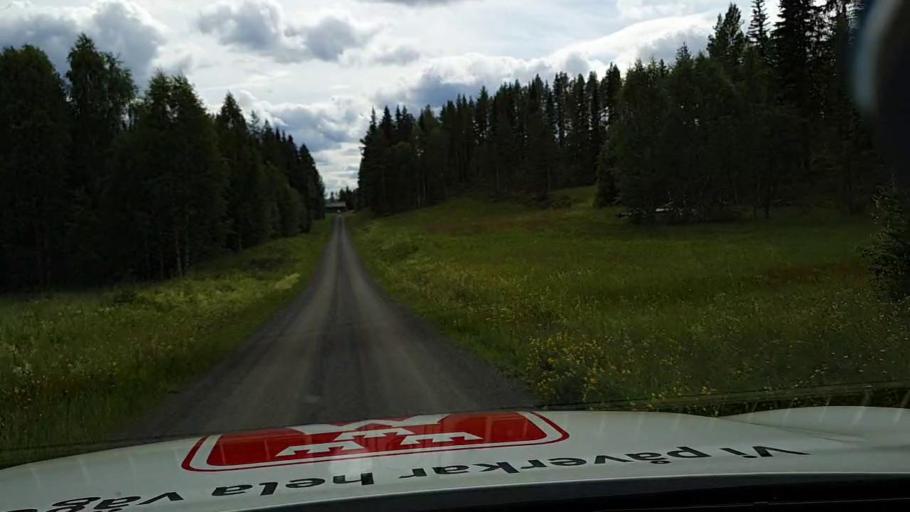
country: SE
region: Jaemtland
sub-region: OEstersunds Kommun
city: Lit
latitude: 63.2833
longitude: 15.2416
